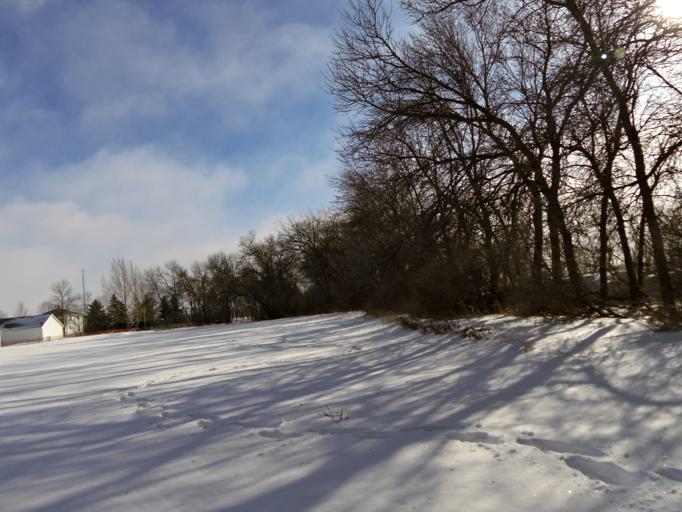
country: US
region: North Dakota
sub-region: Walsh County
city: Grafton
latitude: 48.3990
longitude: -97.2108
